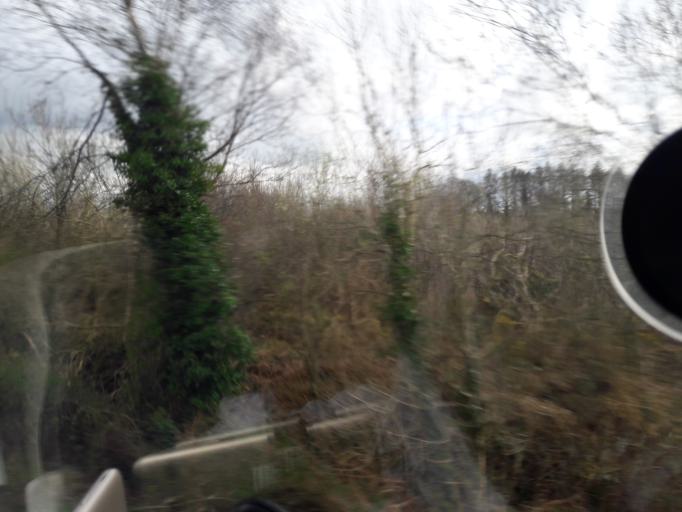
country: IE
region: Leinster
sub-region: An Iarmhi
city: An Muileann gCearr
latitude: 53.5017
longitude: -7.2661
